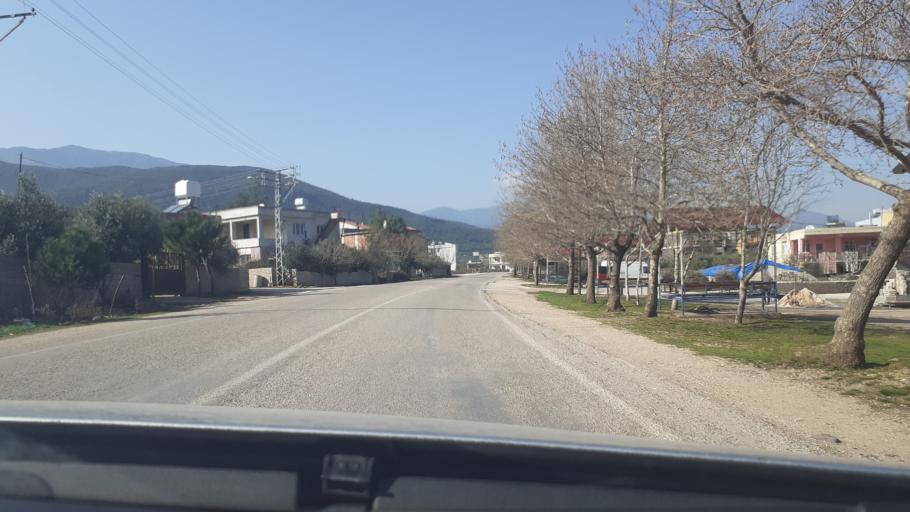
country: TR
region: Hatay
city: Aktepe
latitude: 36.7094
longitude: 36.4868
